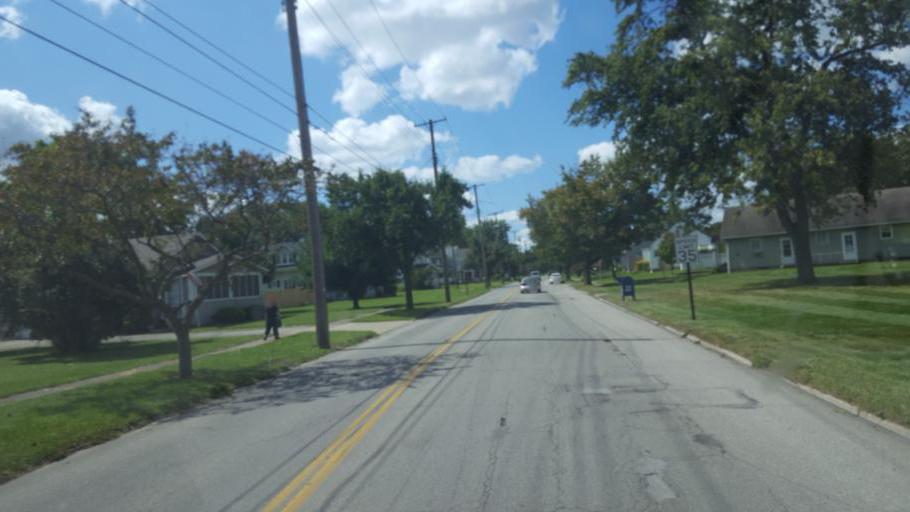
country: US
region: Ohio
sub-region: Ashland County
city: Ashland
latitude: 40.8720
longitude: -82.2964
